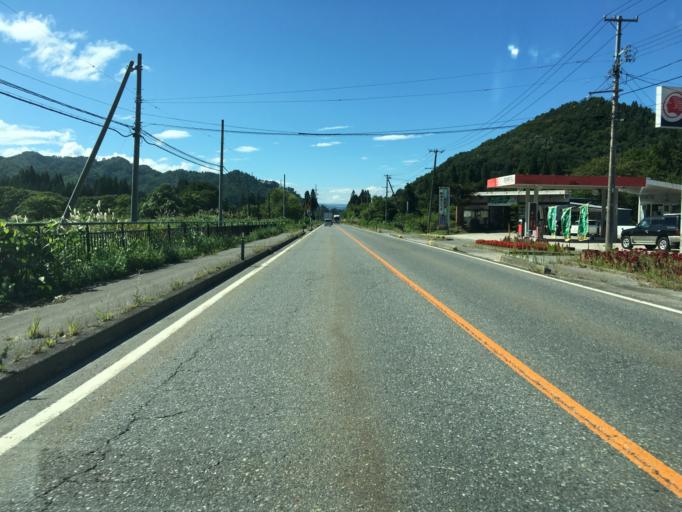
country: JP
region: Yamagata
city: Yonezawa
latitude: 37.8846
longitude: 140.1880
